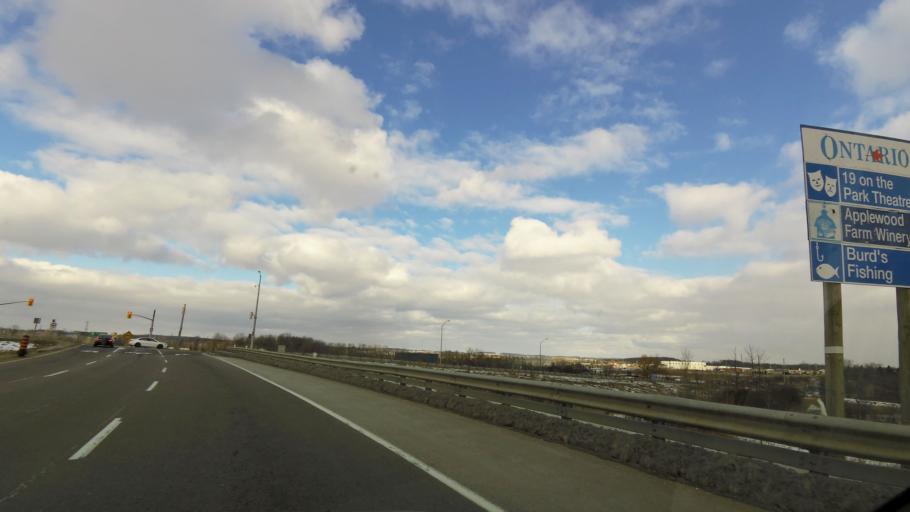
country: CA
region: Ontario
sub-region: York
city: Richmond Hill
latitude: 43.9395
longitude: -79.3877
